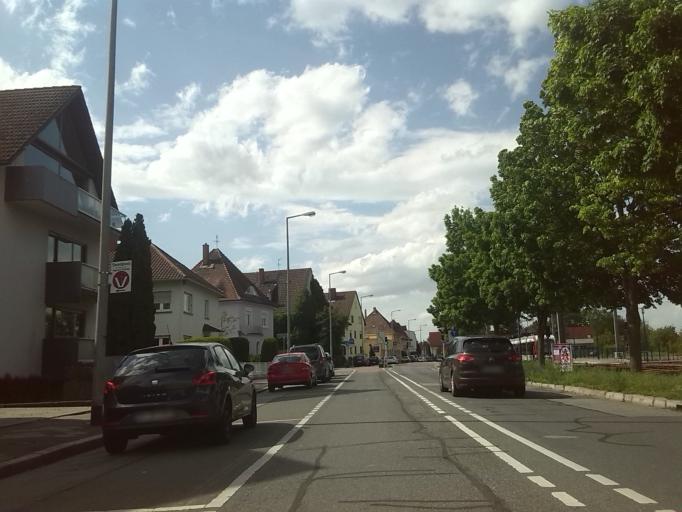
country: DE
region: Baden-Wuerttemberg
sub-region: Karlsruhe Region
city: Ilvesheim
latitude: 49.4613
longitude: 8.5705
